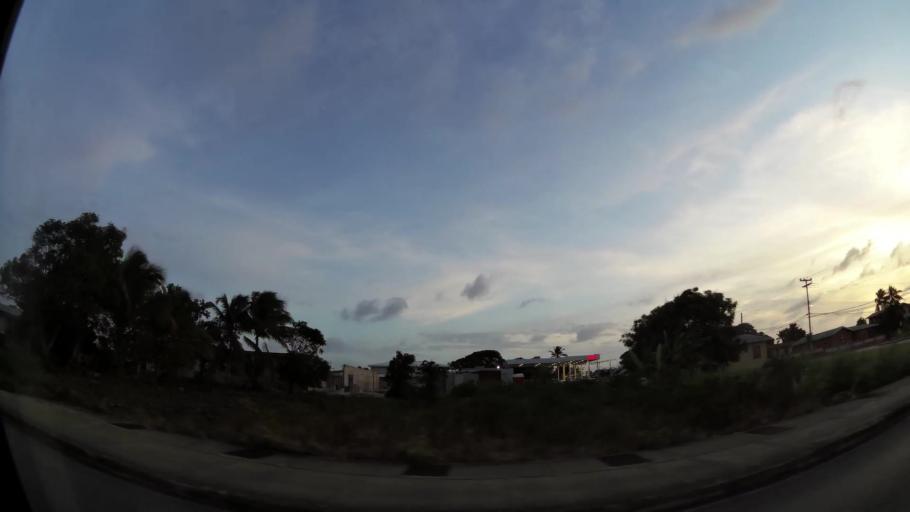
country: BB
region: Saint Philip
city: Crane
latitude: 13.1050
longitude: -59.4652
